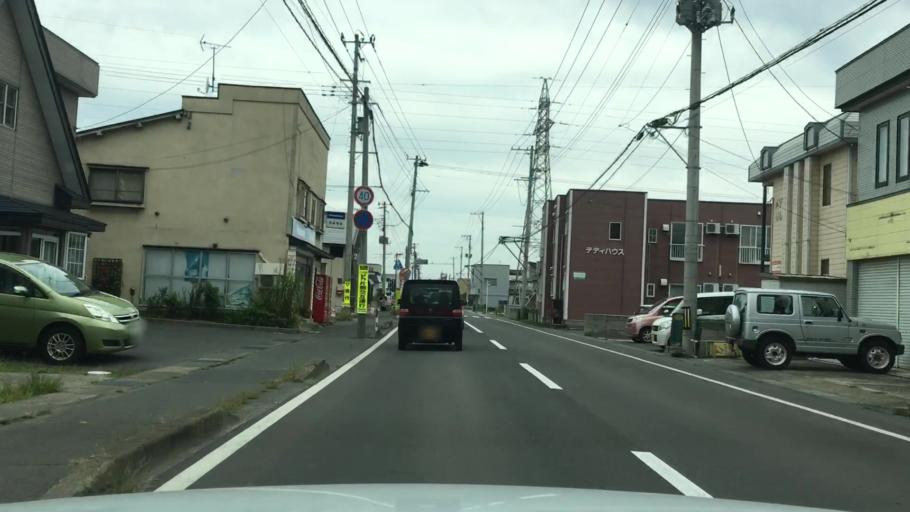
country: JP
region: Aomori
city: Hirosaki
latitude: 40.6253
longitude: 140.4559
